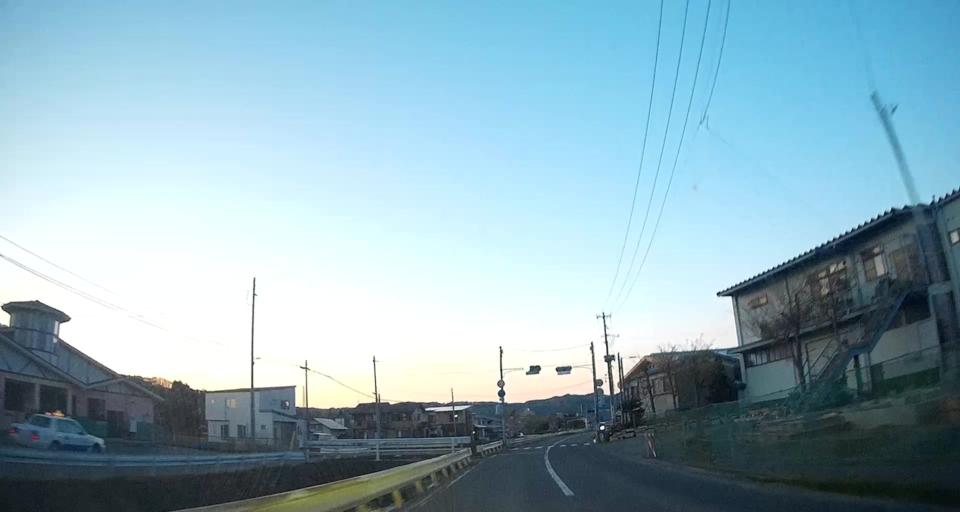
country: JP
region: Aomori
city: Hachinohe
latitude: 40.1836
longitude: 141.7721
